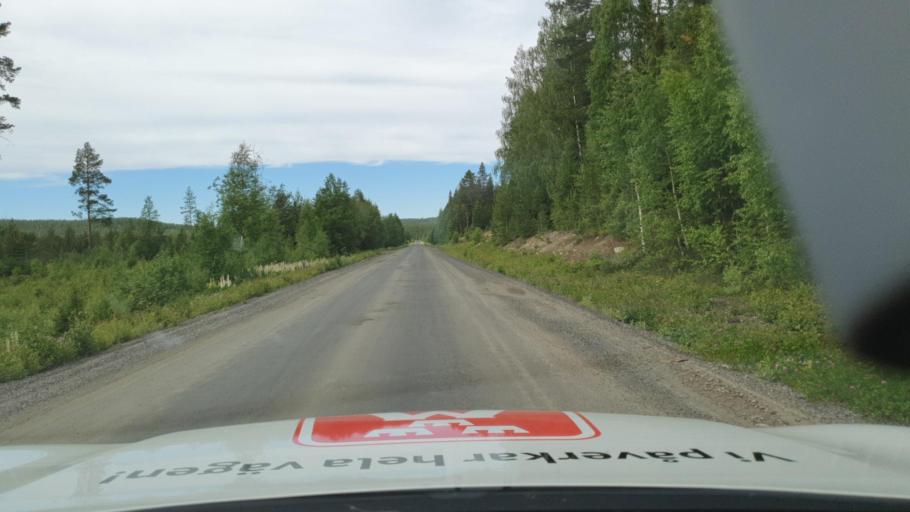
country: SE
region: Vaesterbotten
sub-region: Skelleftea Kommun
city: Burtraesk
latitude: 64.3747
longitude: 20.3631
